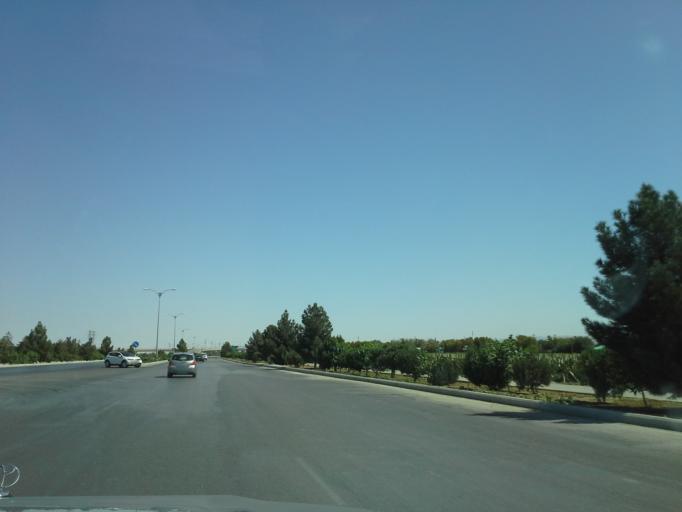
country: TM
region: Ahal
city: Annau
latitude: 37.9157
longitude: 58.4731
